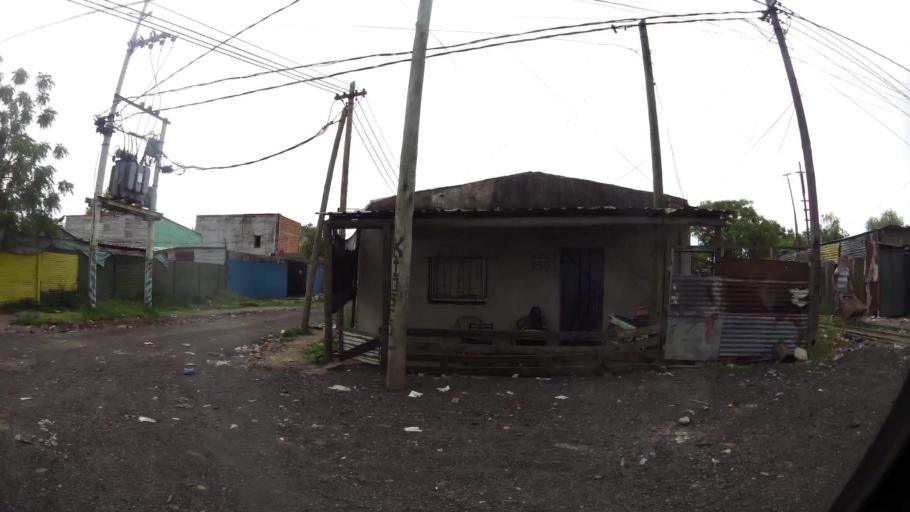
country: AR
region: Buenos Aires
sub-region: Partido de Avellaneda
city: Avellaneda
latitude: -34.6535
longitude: -58.3566
